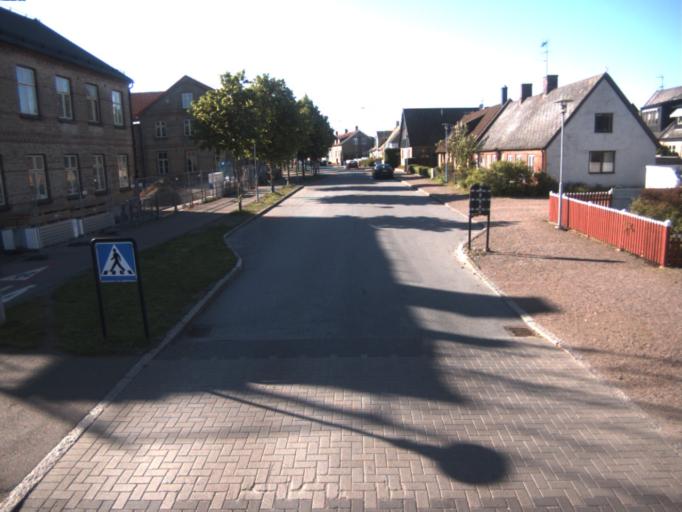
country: SE
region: Skane
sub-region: Helsingborg
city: Rydeback
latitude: 55.9970
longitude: 12.7401
